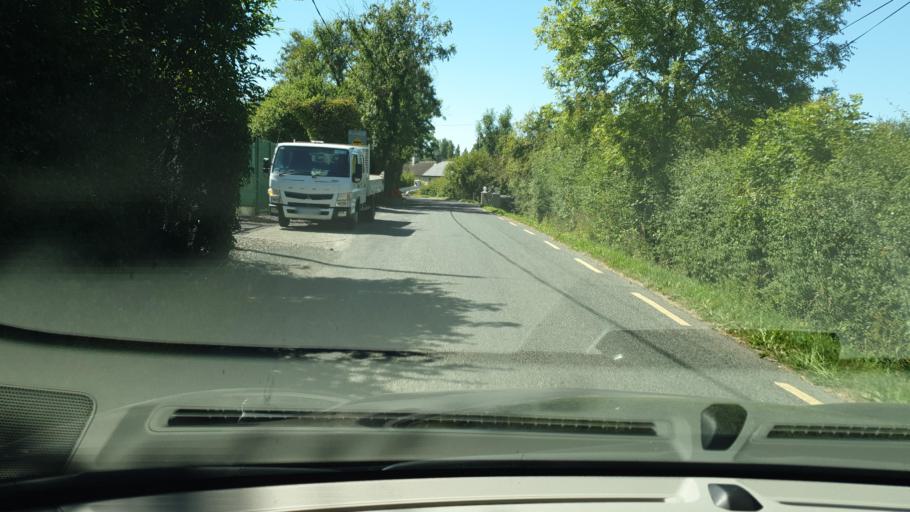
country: IE
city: Confey
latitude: 53.3768
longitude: -6.4796
